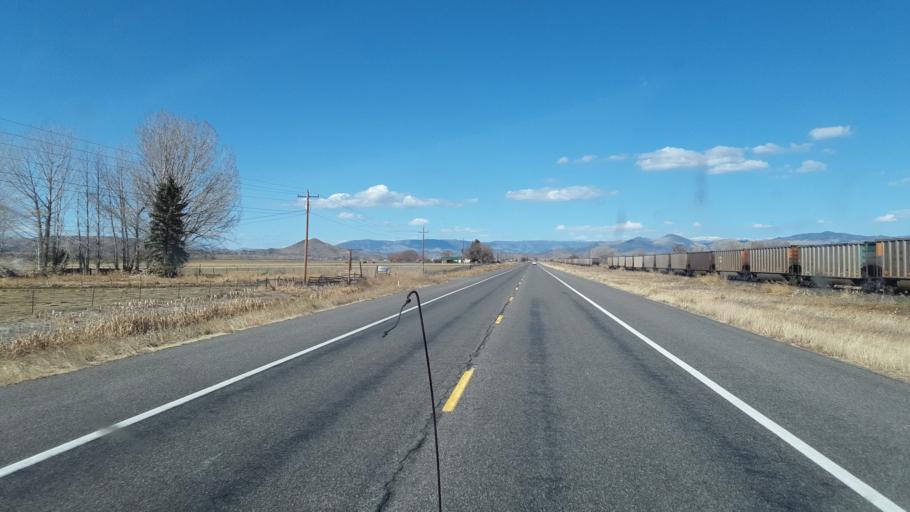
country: US
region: Colorado
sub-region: Rio Grande County
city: Del Norte
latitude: 37.6594
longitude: -106.2938
